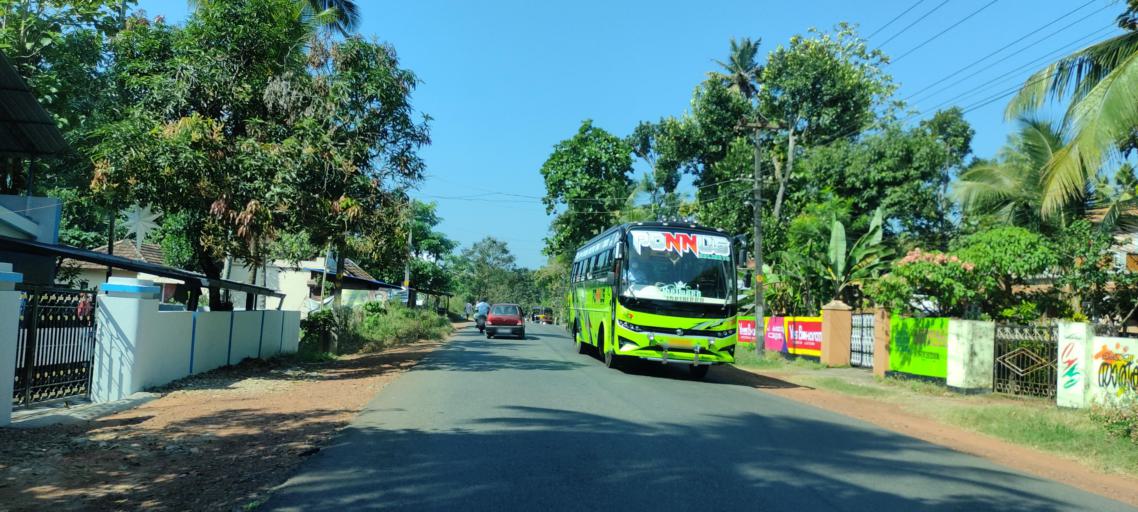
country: IN
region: Kerala
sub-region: Kollam
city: Panmana
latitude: 9.0432
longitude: 76.6191
